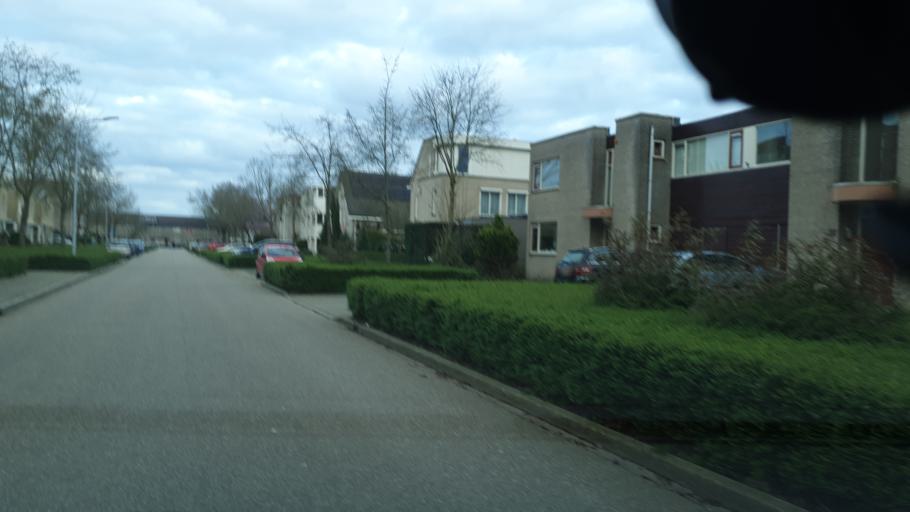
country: NL
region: Gelderland
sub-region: Gemeente Duiven
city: Duiven
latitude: 51.9506
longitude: 6.0313
